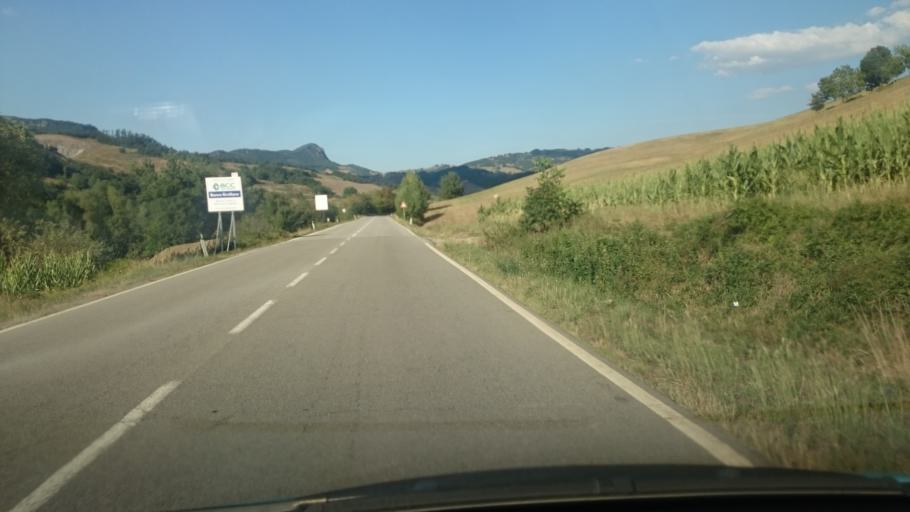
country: IT
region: Emilia-Romagna
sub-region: Provincia di Reggio Emilia
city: Carpineti
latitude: 44.4122
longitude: 10.5267
